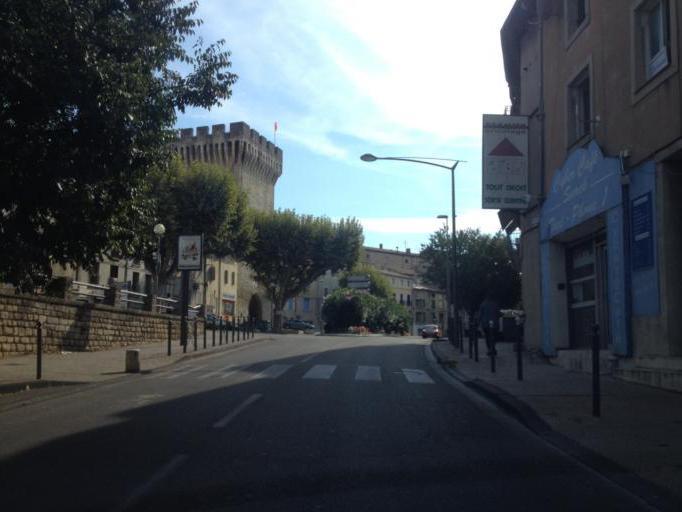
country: FR
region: Provence-Alpes-Cote d'Azur
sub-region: Departement du Vaucluse
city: Carpentras
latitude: 44.0573
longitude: 5.0478
